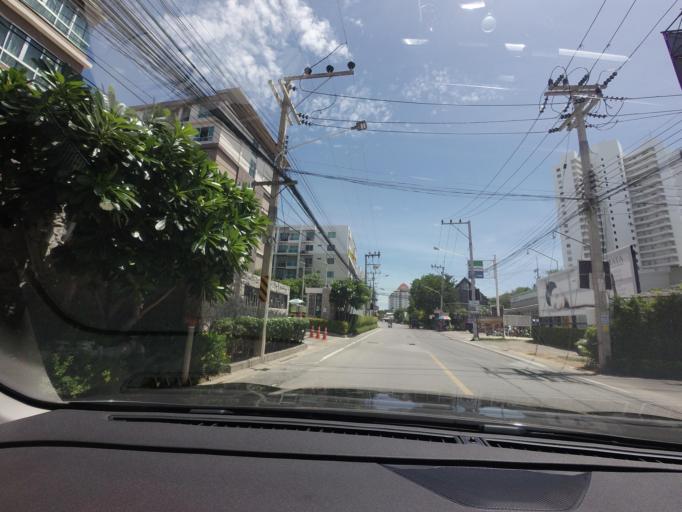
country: TH
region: Prachuap Khiri Khan
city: Hua Hin
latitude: 12.5145
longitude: 99.9761
